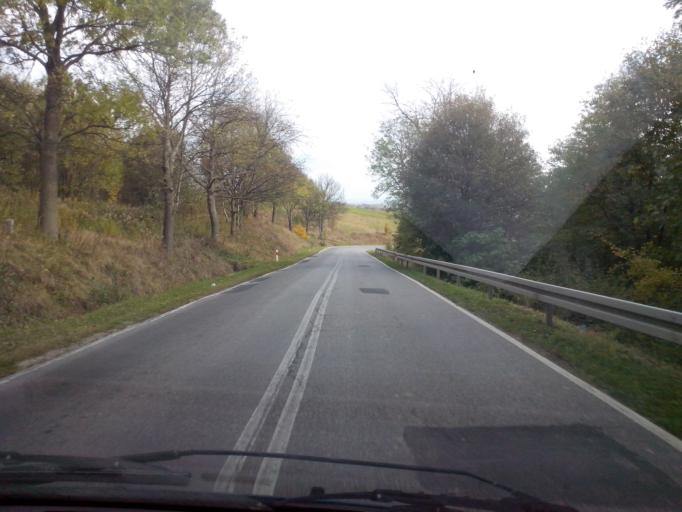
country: PL
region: Subcarpathian Voivodeship
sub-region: Powiat ropczycko-sedziszowski
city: Wielopole Skrzynskie
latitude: 49.9141
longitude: 21.6159
